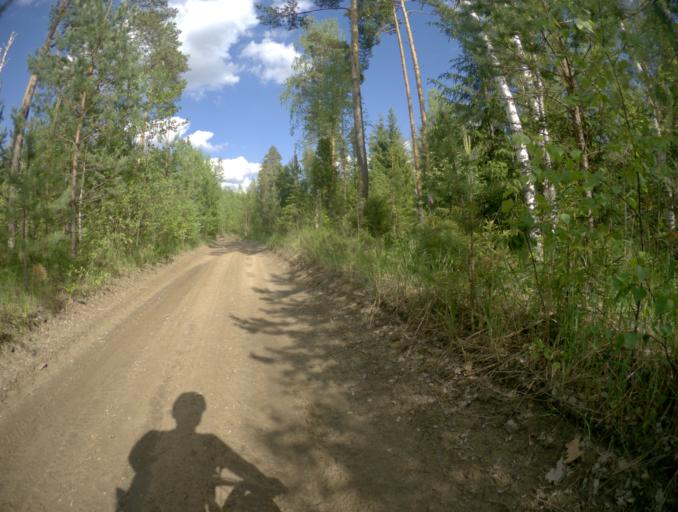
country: RU
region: Vladimir
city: Zolotkovo
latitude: 55.3297
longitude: 40.9670
